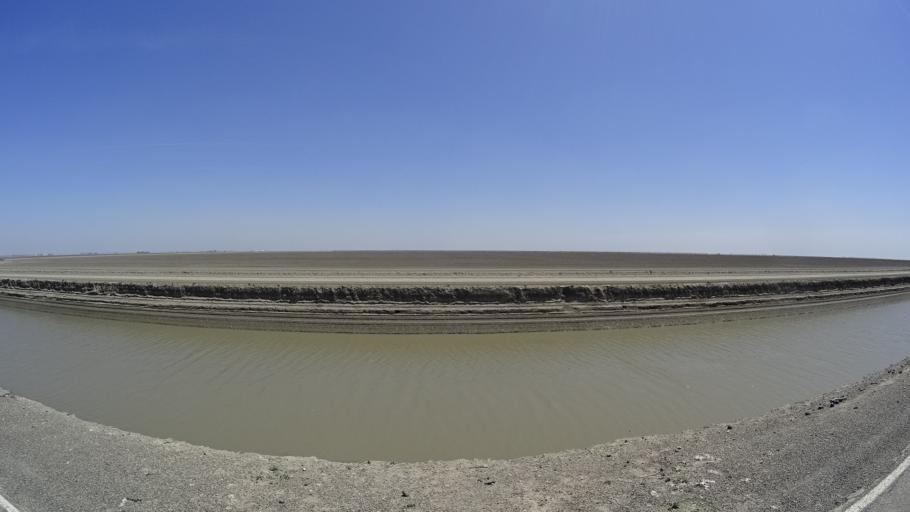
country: US
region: California
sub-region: Kings County
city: Corcoran
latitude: 35.9892
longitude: -119.6424
